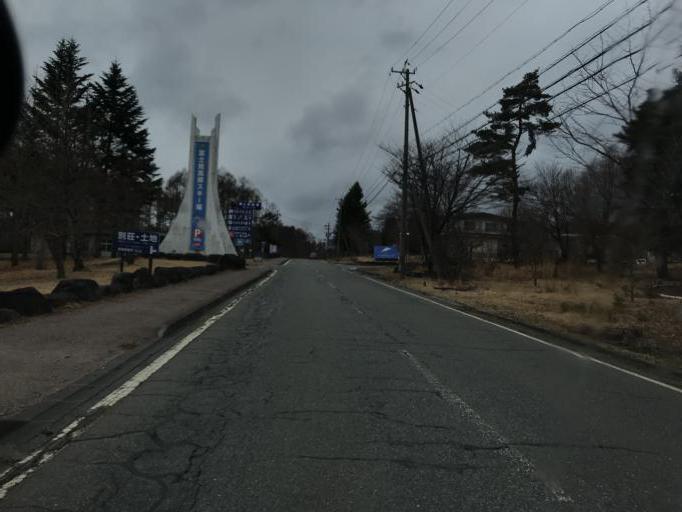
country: JP
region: Nagano
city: Chino
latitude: 35.9156
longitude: 138.3061
